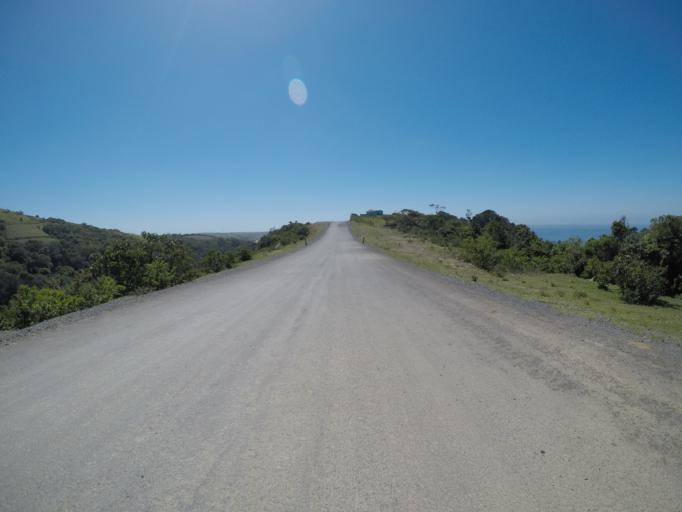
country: ZA
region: Eastern Cape
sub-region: OR Tambo District Municipality
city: Libode
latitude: -31.9939
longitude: 29.1312
